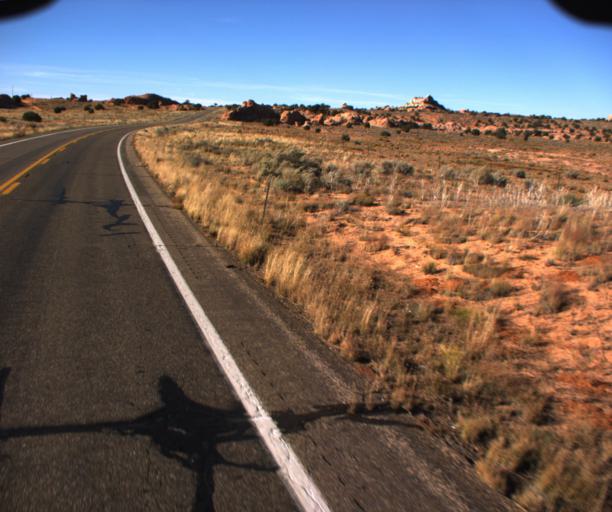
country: US
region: Arizona
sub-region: Coconino County
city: Kaibito
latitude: 36.6218
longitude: -111.2001
